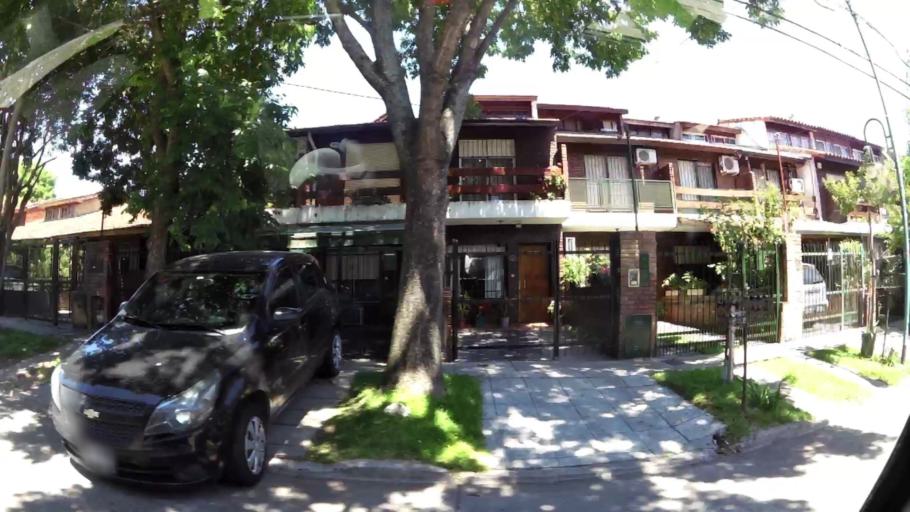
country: AR
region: Buenos Aires
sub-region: Partido de Vicente Lopez
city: Olivos
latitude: -34.5103
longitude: -58.5150
